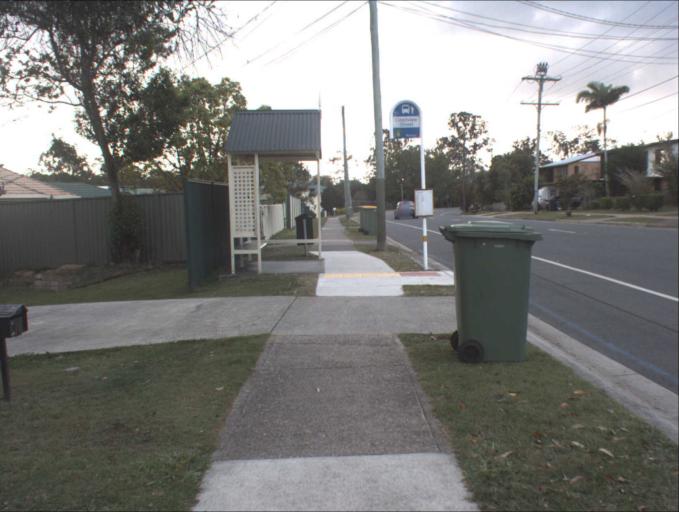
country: AU
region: Queensland
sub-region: Logan
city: Waterford West
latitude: -27.6818
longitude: 153.1322
